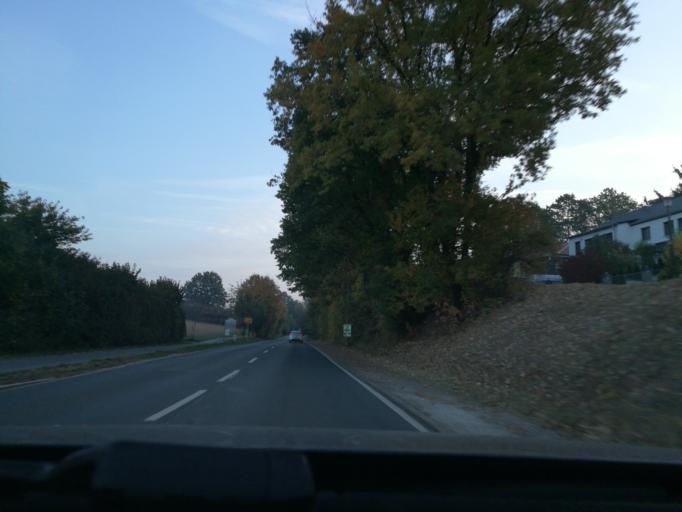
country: DE
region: Bavaria
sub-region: Regierungsbezirk Mittelfranken
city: Veitsbronn
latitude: 49.5129
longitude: 10.8907
